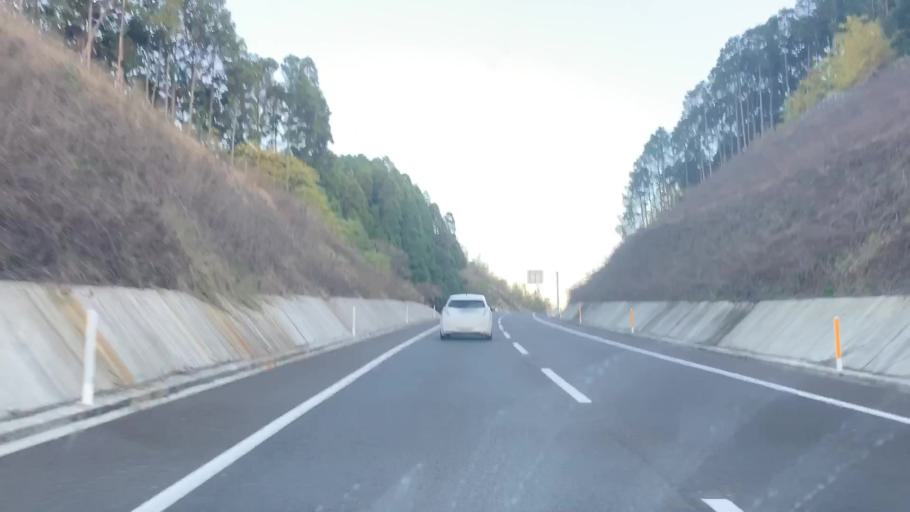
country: JP
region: Saga Prefecture
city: Takeocho-takeo
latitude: 33.2568
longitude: 129.9797
